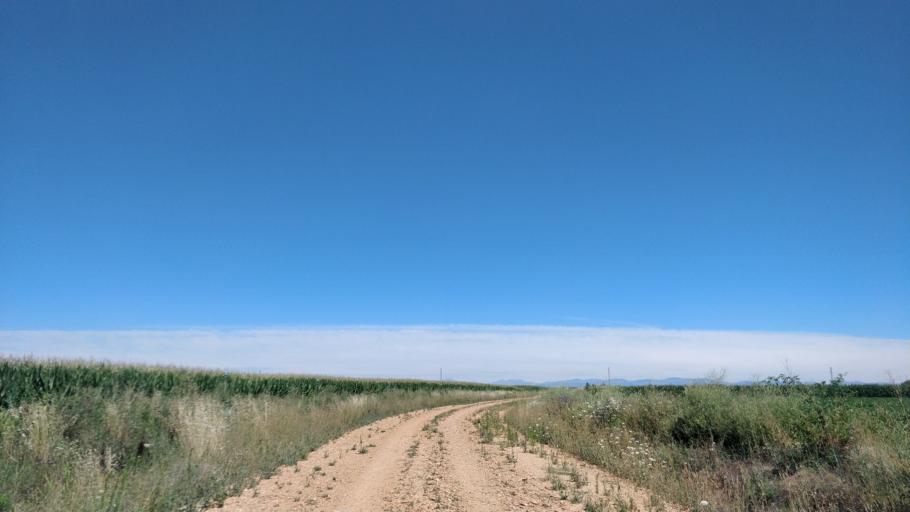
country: ES
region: Castille and Leon
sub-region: Provincia de Leon
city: Bustillo del Paramo
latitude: 42.4540
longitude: -5.8165
